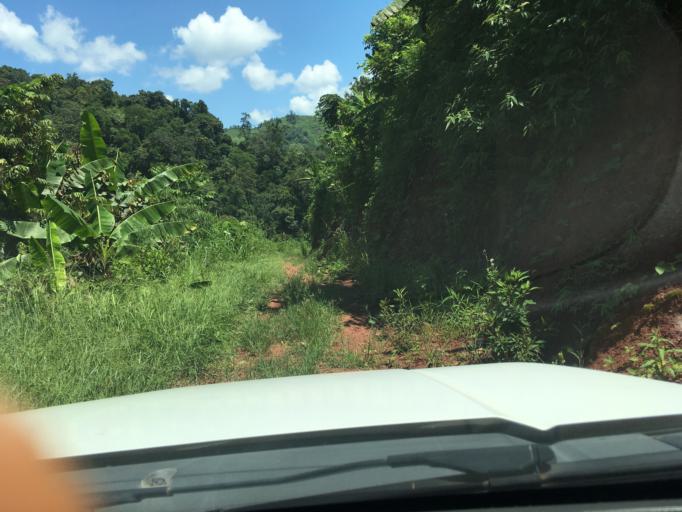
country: LA
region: Phongsali
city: Phongsali
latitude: 21.7917
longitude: 101.8625
